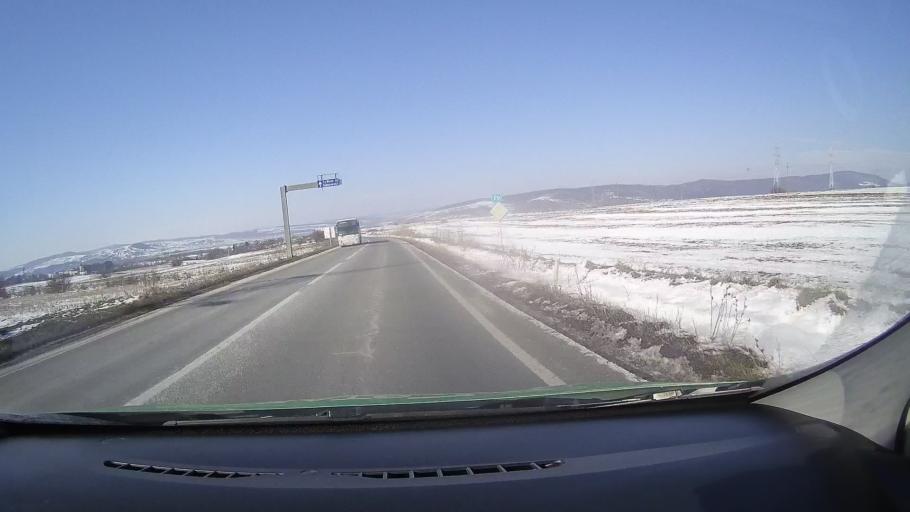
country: RO
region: Brasov
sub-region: Comuna Hoghiz
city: Hoghiz
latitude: 45.9828
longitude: 25.3234
